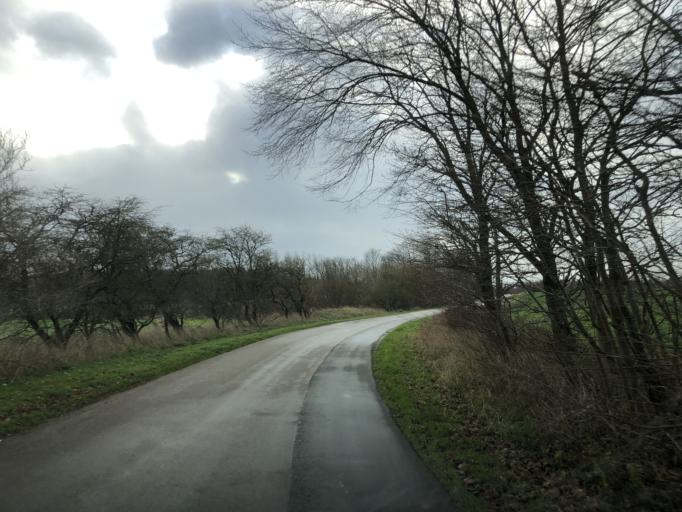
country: DK
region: North Denmark
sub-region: Rebild Kommune
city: Stovring
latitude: 56.9177
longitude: 9.8016
